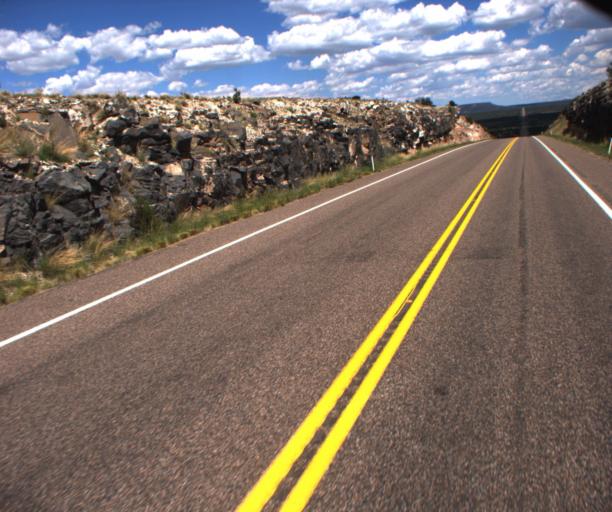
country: US
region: Arizona
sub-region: Apache County
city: Springerville
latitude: 34.1497
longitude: -109.1777
